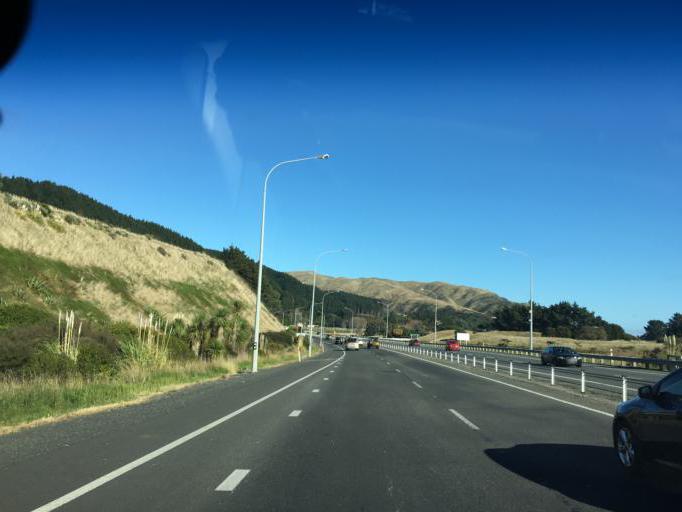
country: NZ
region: Wellington
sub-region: Kapiti Coast District
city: Paraparaumu
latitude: -40.9742
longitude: 174.9802
